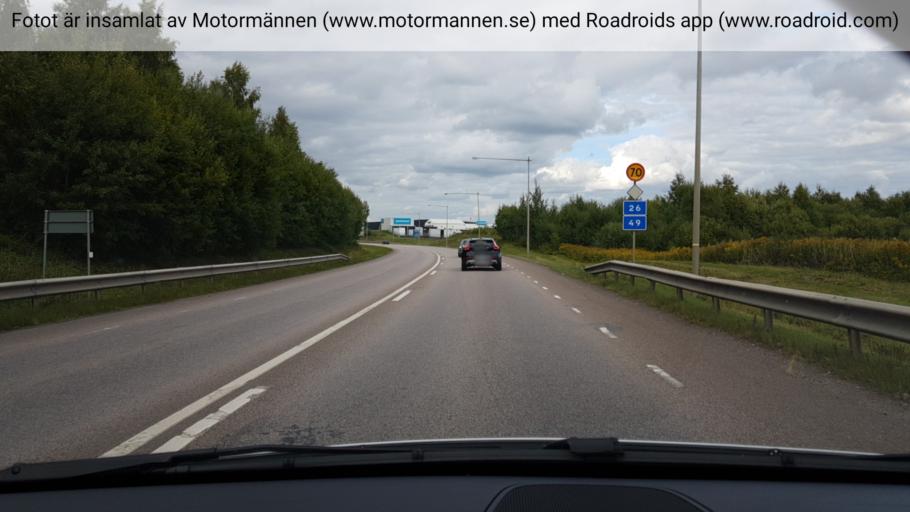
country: SE
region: Vaestra Goetaland
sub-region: Skovde Kommun
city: Skoevde
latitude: 58.3829
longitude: 13.8734
